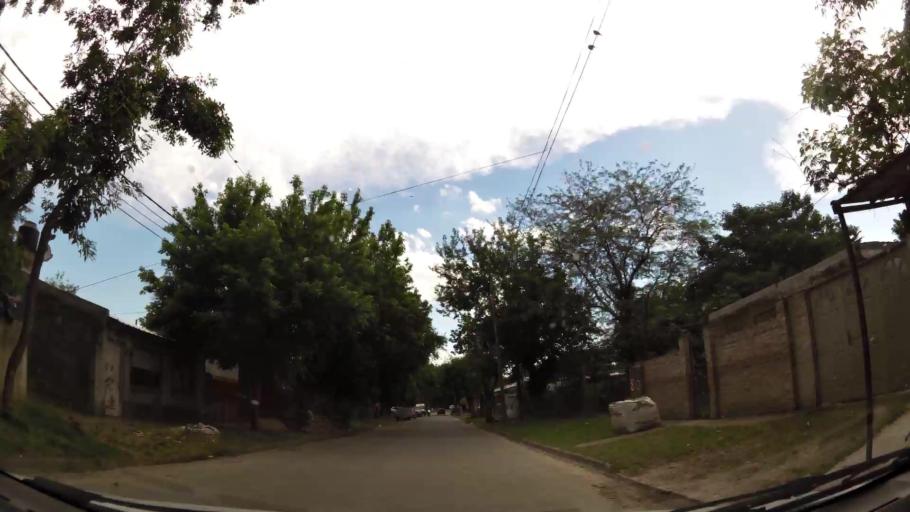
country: AR
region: Buenos Aires
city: Ituzaingo
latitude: -34.6338
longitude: -58.6954
